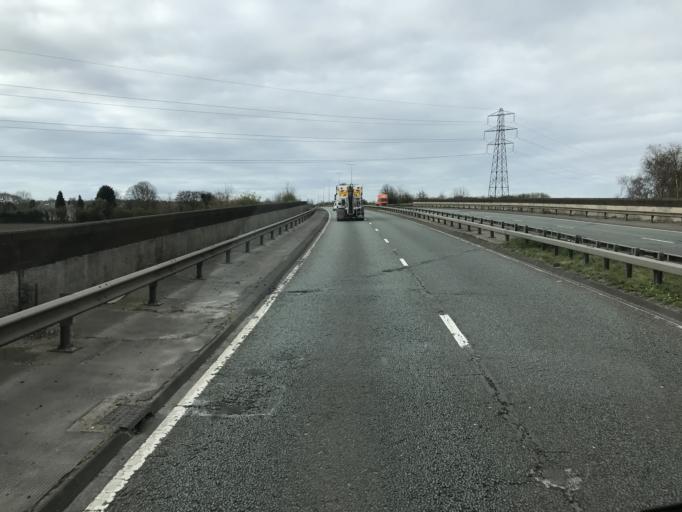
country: GB
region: England
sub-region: Borough of Halton
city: Hale
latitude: 53.3556
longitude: -2.8087
